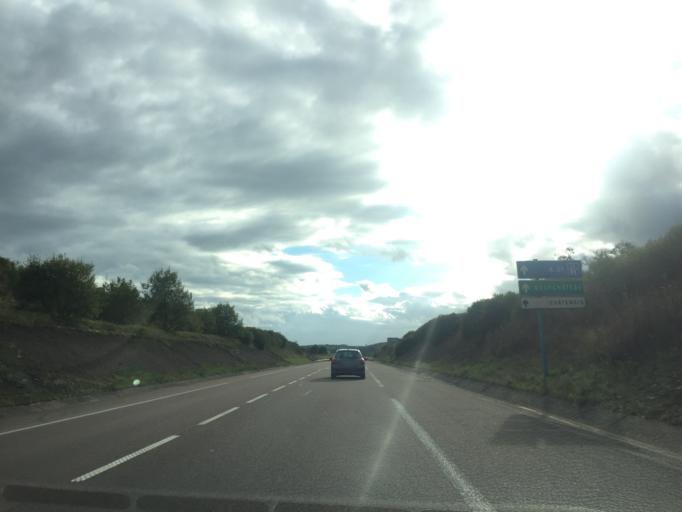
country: FR
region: Lorraine
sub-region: Departement des Vosges
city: Chatenois
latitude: 48.2964
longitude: 5.9063
